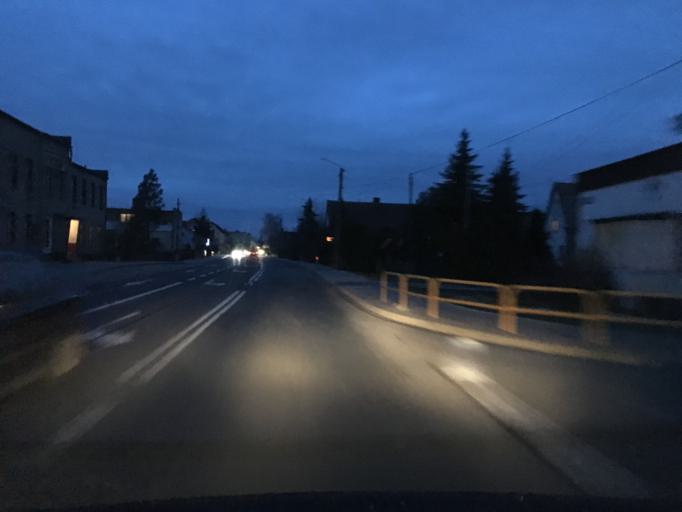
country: PL
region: Opole Voivodeship
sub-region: Powiat brzeski
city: Losiow
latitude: 50.7903
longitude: 17.5673
